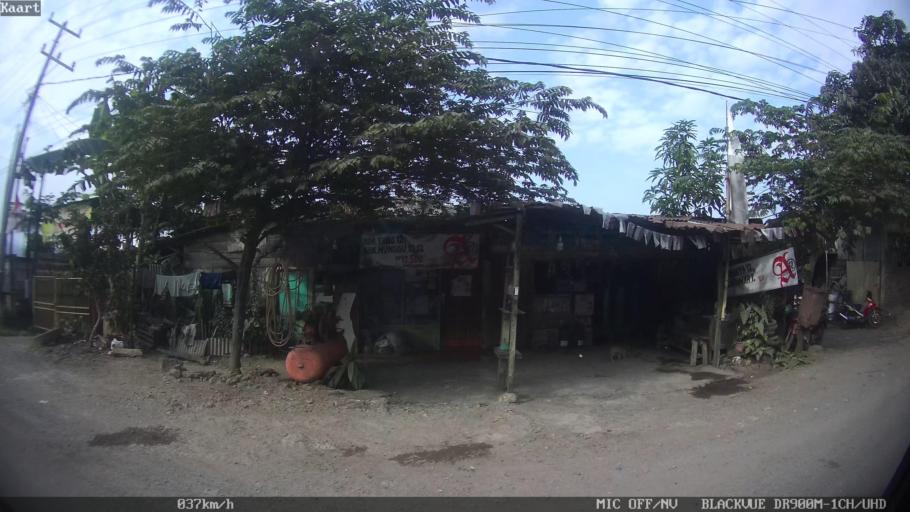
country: ID
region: Lampung
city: Panjang
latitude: -5.4605
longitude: 105.3194
